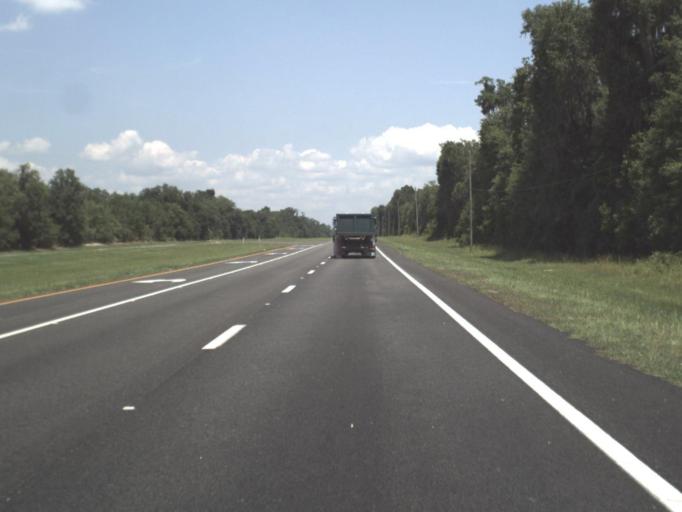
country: US
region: Florida
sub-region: Alachua County
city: Gainesville
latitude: 29.6088
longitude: -82.2366
